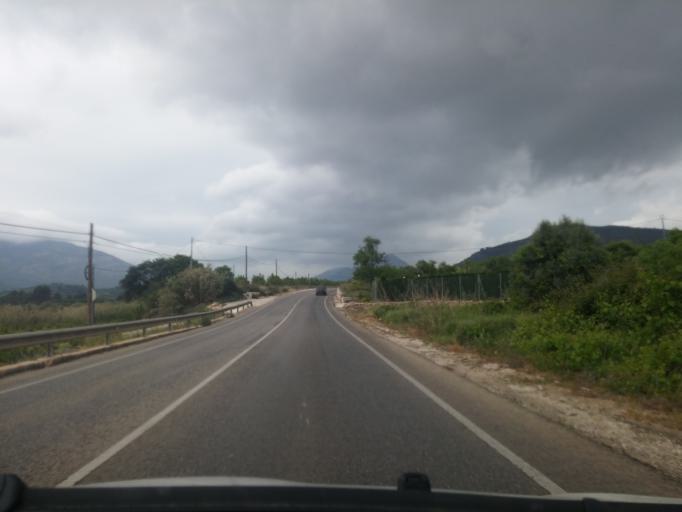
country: ES
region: Valencia
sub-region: Provincia de Alicante
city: Alcalali
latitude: 38.7467
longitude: -0.0264
